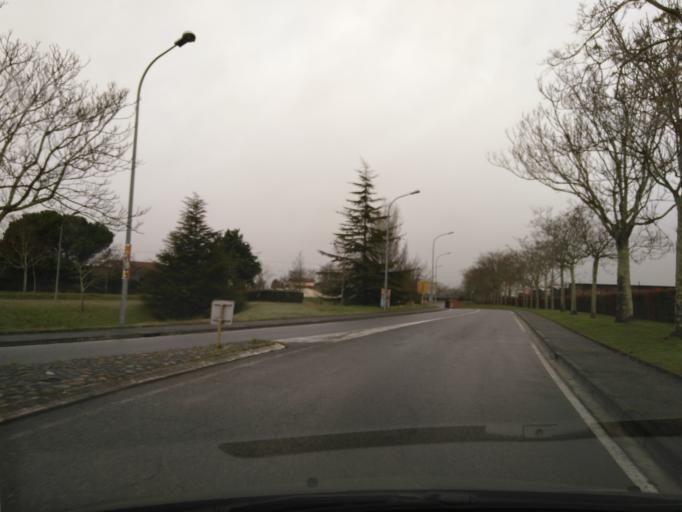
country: FR
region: Midi-Pyrenees
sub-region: Departement de la Haute-Garonne
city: Carbonne
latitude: 43.3023
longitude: 1.2203
